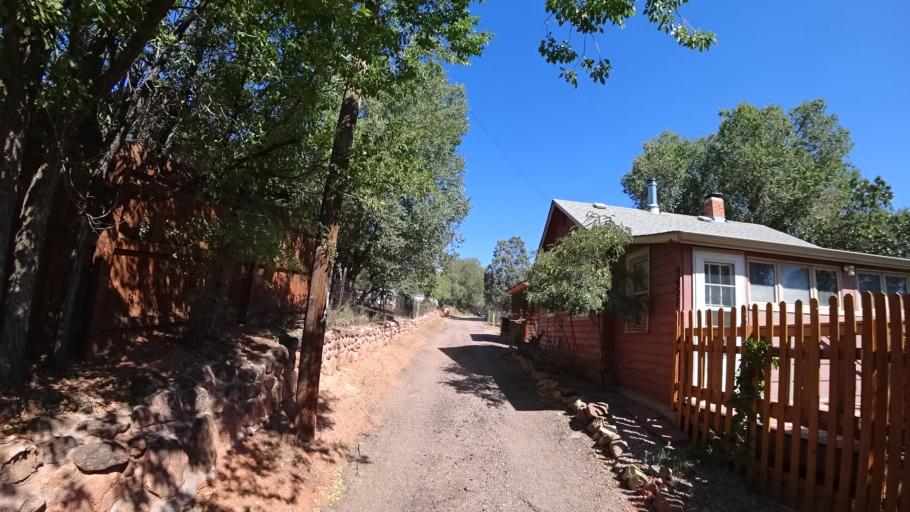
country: US
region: Colorado
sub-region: El Paso County
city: Manitou Springs
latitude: 38.8572
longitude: -104.8804
